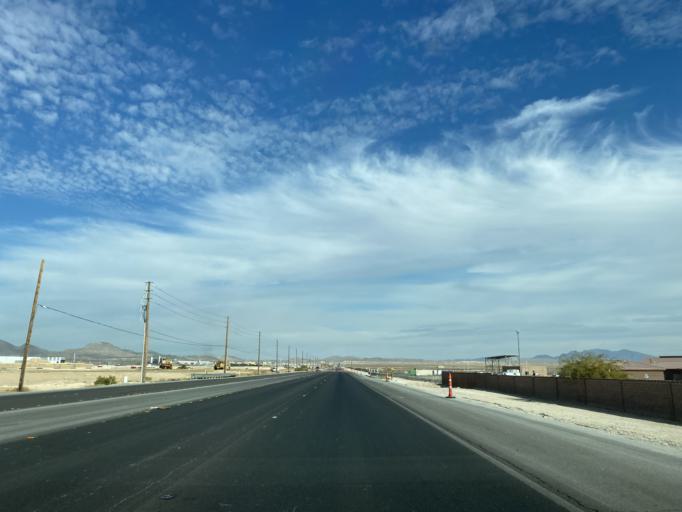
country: US
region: Nevada
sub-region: Clark County
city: Nellis Air Force Base
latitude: 36.2533
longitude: -115.0324
